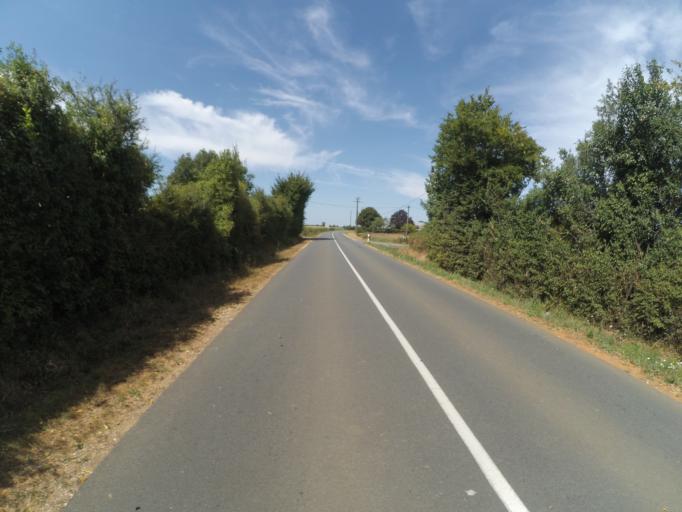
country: FR
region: Poitou-Charentes
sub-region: Departement de la Vienne
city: Availles-Limouzine
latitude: 46.1208
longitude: 0.5619
